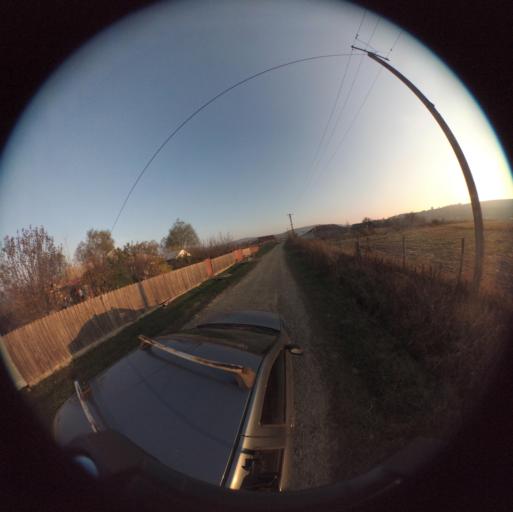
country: RO
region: Vaslui
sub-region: Comuna Bacesti
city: Bacesti
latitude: 46.8326
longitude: 27.2453
